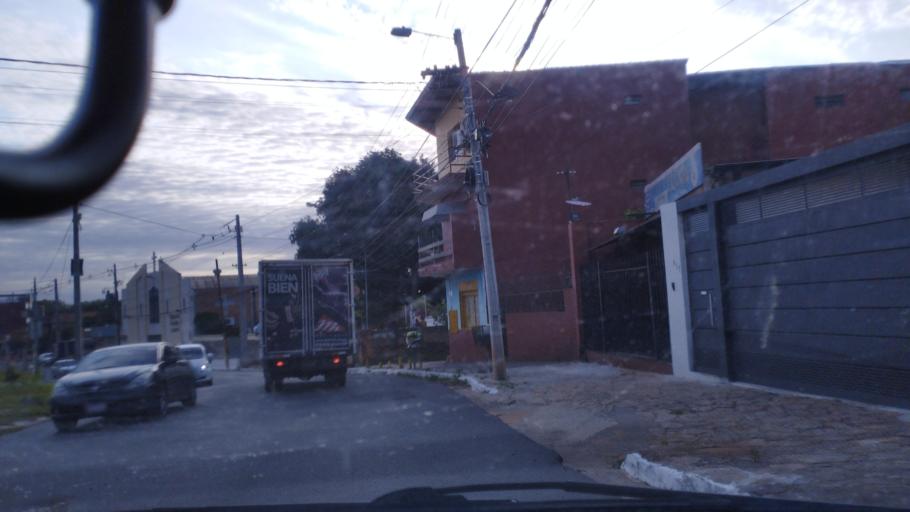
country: PY
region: Central
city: Fernando de la Mora
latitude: -25.3177
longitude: -57.5496
